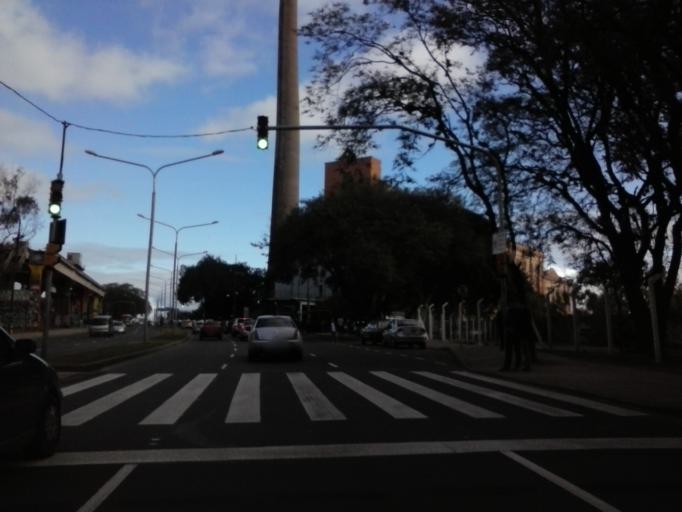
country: BR
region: Rio Grande do Sul
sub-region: Porto Alegre
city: Porto Alegre
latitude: -30.0331
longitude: -51.2399
